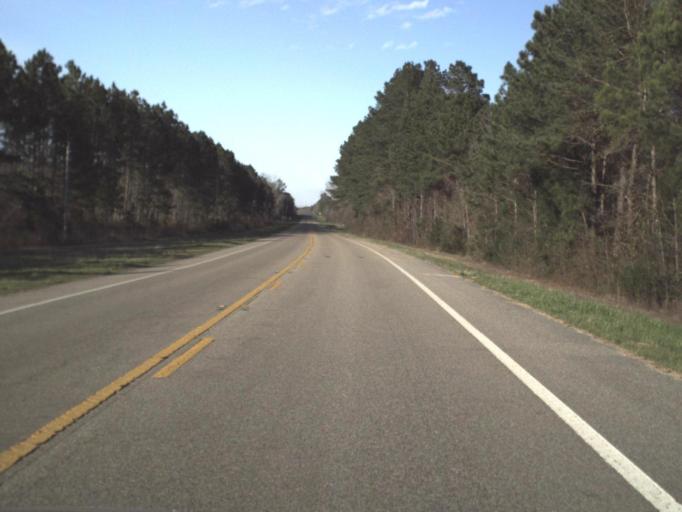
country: US
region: Florida
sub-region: Jackson County
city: Marianna
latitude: 30.6926
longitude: -85.2346
